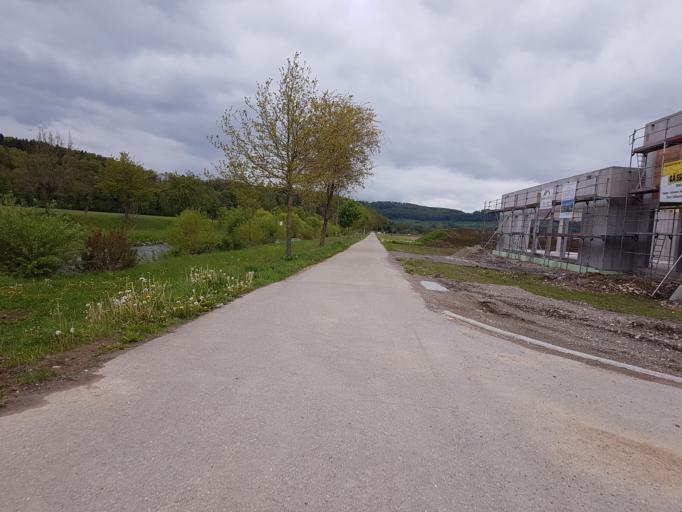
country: DE
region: Baden-Wuerttemberg
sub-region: Freiburg Region
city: Wutoschingen
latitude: 47.6388
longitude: 8.3471
